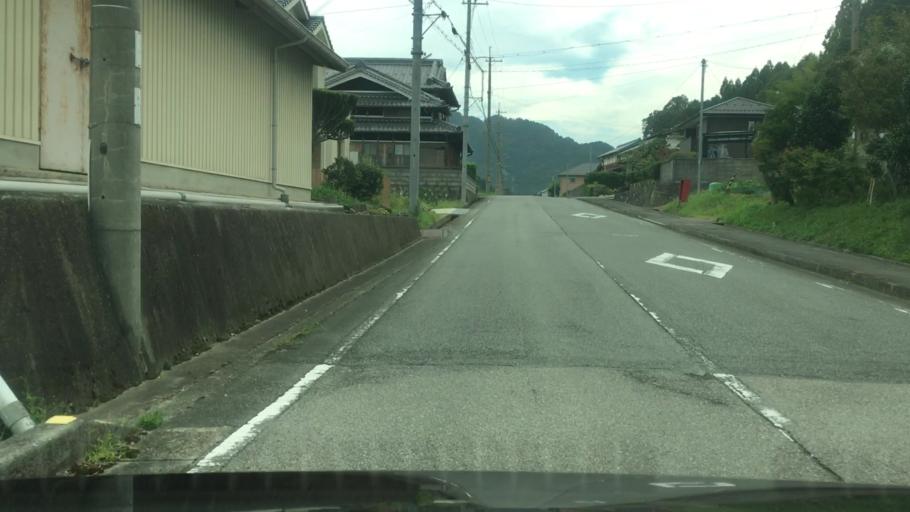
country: JP
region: Hyogo
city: Sasayama
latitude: 35.0724
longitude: 135.1837
